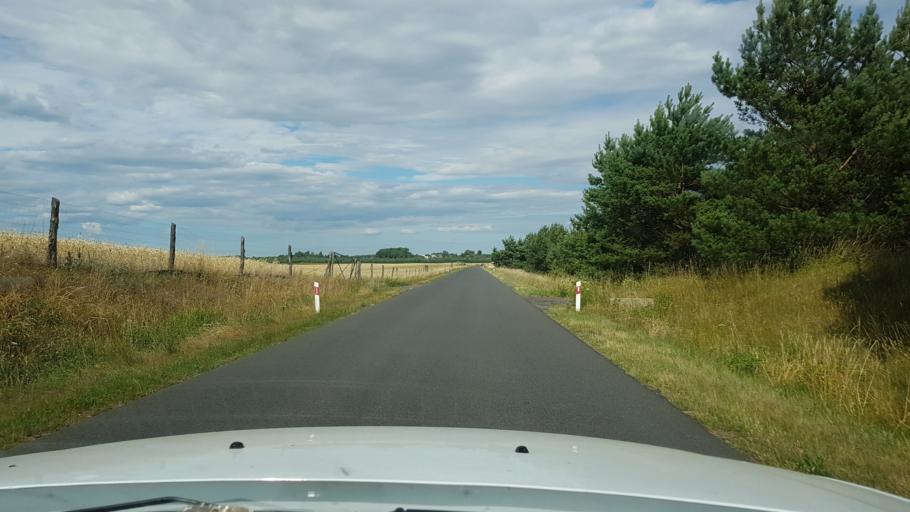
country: PL
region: West Pomeranian Voivodeship
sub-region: Powiat drawski
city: Wierzchowo
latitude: 53.4278
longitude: 16.0550
